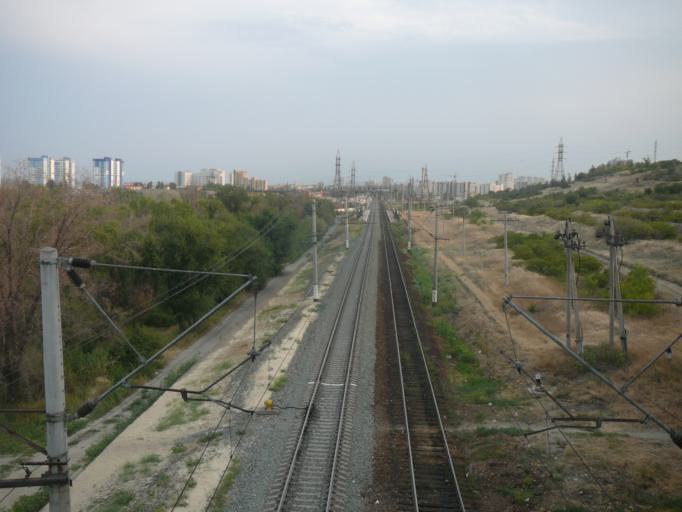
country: RU
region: Volgograd
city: Volgograd
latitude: 48.7405
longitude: 44.5424
